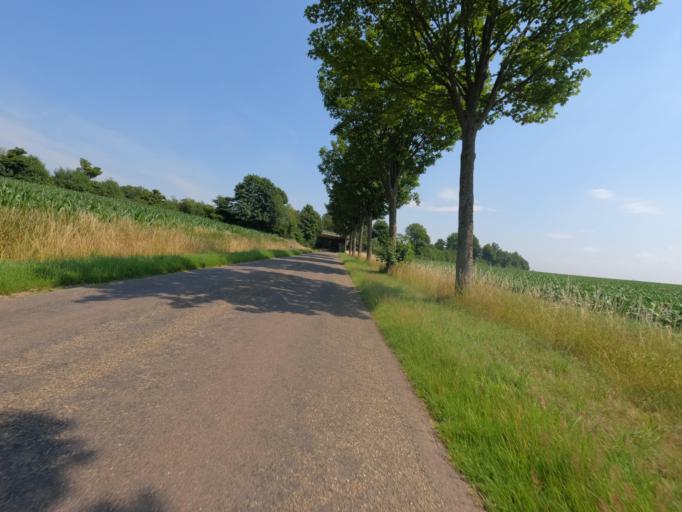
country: DE
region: North Rhine-Westphalia
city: Geilenkirchen
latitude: 50.9678
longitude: 6.0871
